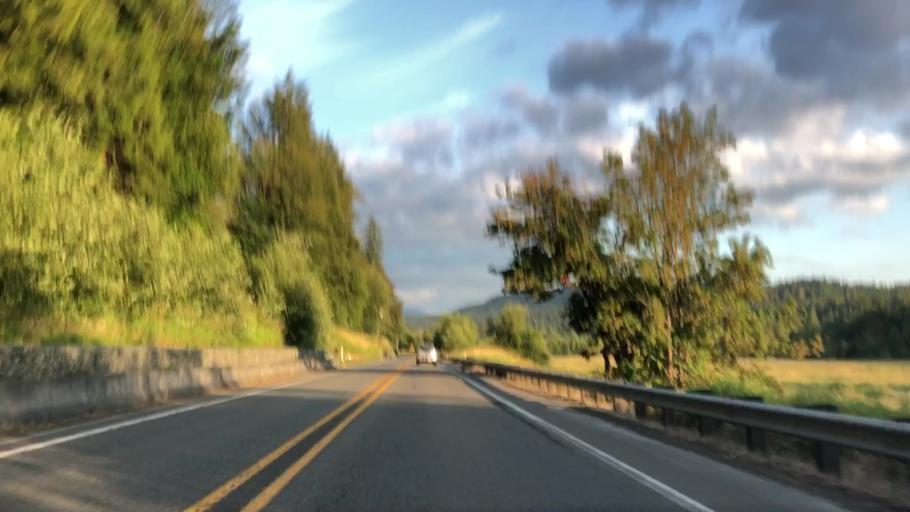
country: US
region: Washington
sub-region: King County
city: Ames Lake
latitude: 47.5929
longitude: -121.9587
